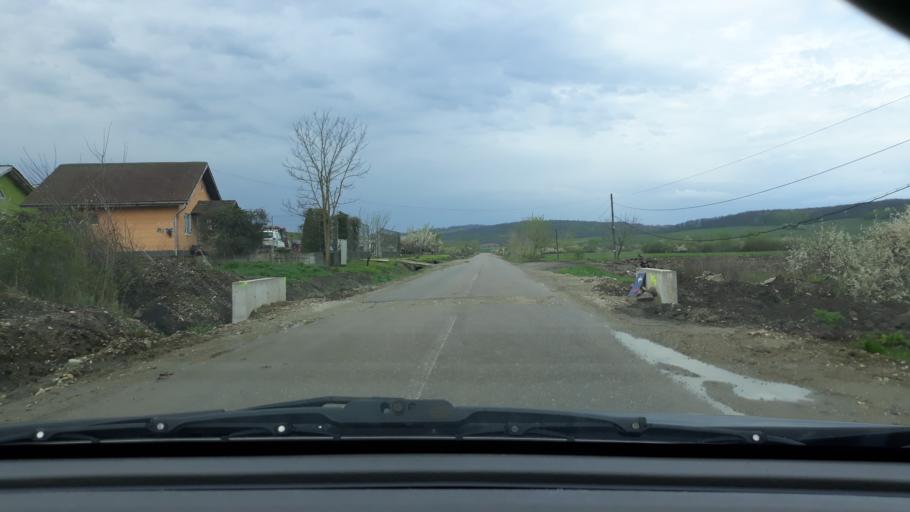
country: RO
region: Salaj
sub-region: Comuna Salatig
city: Salatig
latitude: 47.3894
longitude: 23.1525
